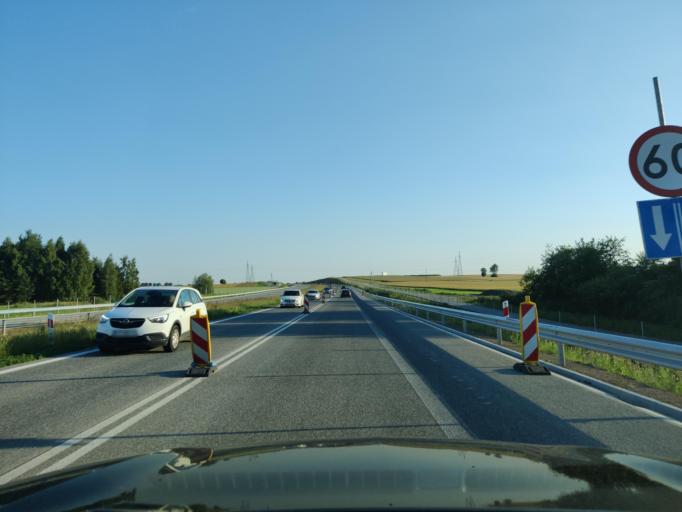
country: PL
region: Masovian Voivodeship
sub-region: Powiat mlawski
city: Mlawa
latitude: 53.1300
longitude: 20.4162
